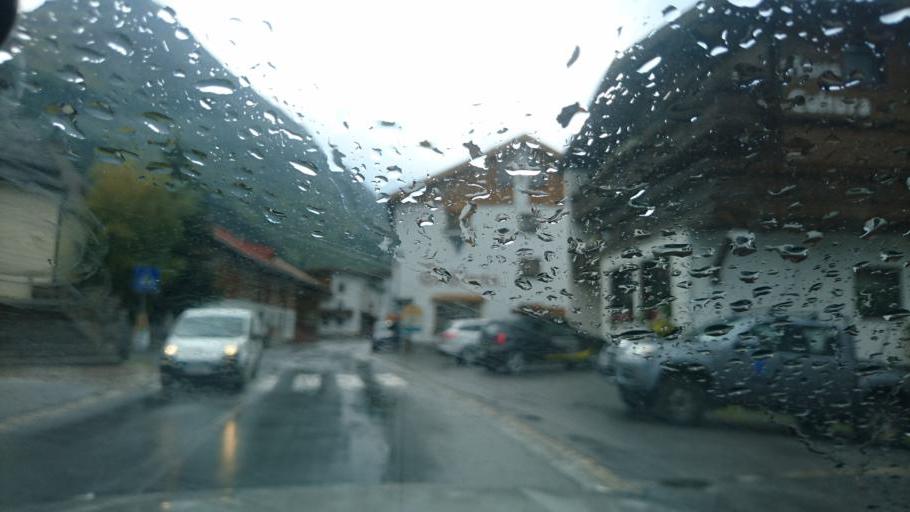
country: AT
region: Tyrol
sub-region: Politischer Bezirk Landeck
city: Galtur
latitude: 46.9688
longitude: 10.1864
